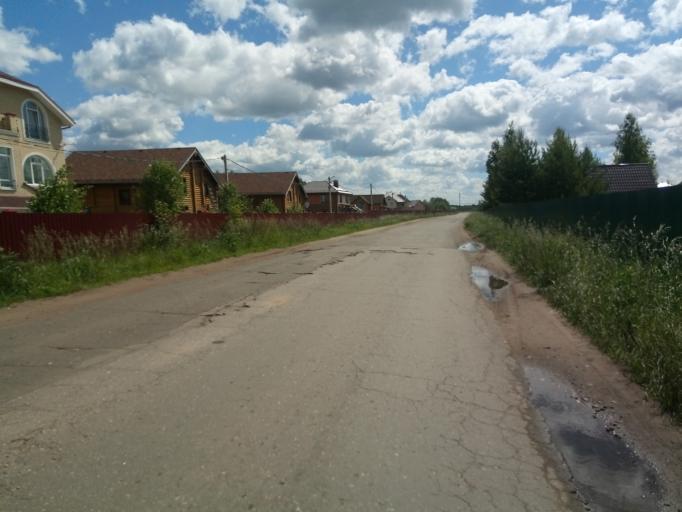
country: RU
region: Jaroslavl
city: Yaroslavl
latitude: 57.6535
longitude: 39.9883
